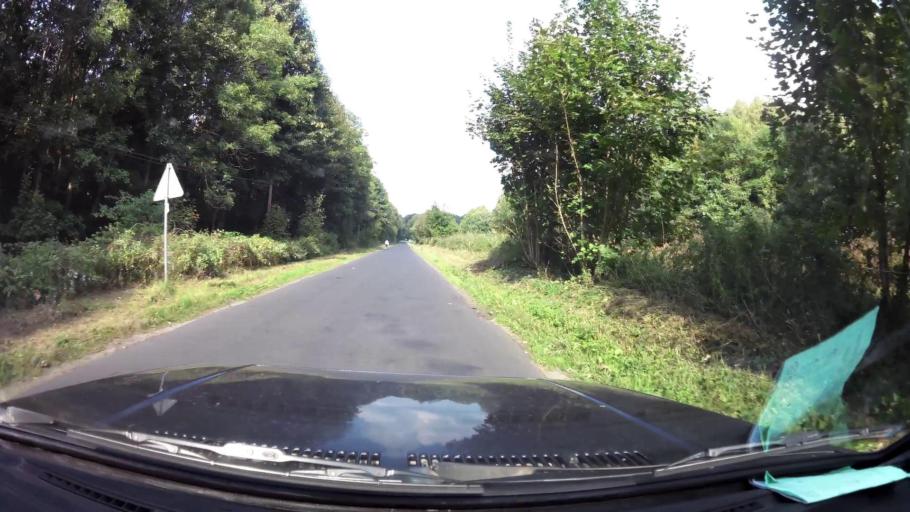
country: PL
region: West Pomeranian Voivodeship
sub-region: Powiat koszalinski
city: Polanow
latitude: 54.1342
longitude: 16.5239
